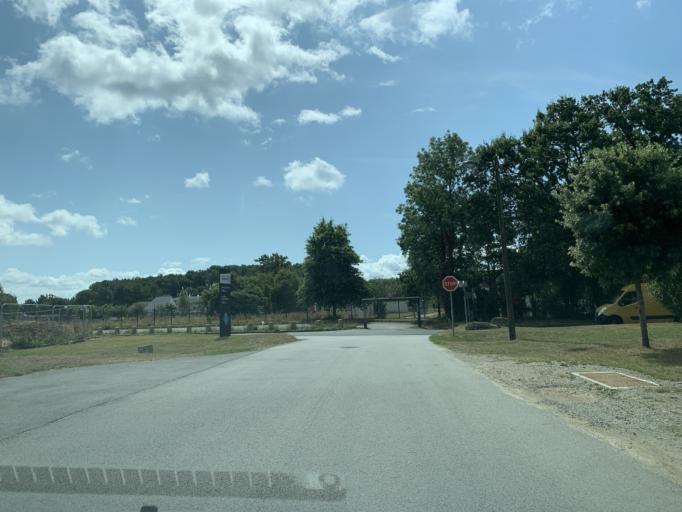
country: FR
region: Brittany
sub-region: Departement du Morbihan
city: Vannes
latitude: 47.6428
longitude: -2.7455
